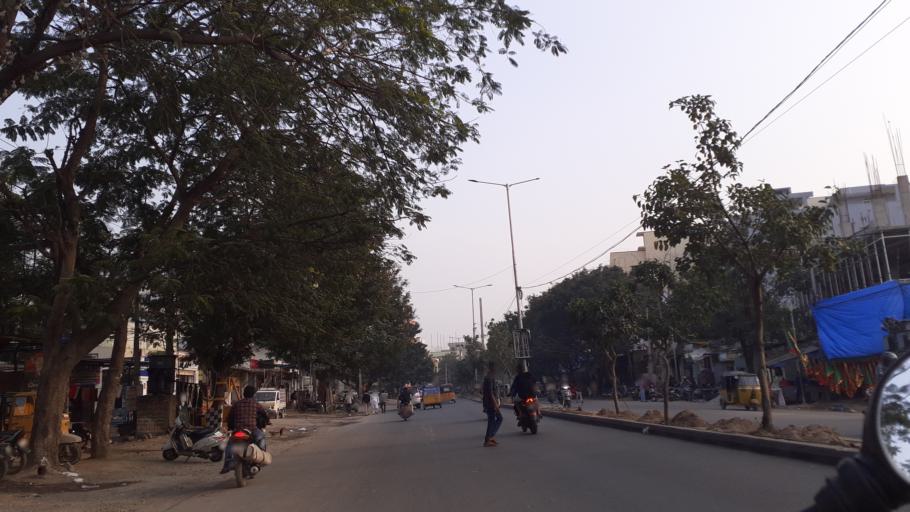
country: IN
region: Telangana
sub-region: Rangareddi
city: Kukatpalli
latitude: 17.4779
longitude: 78.3622
